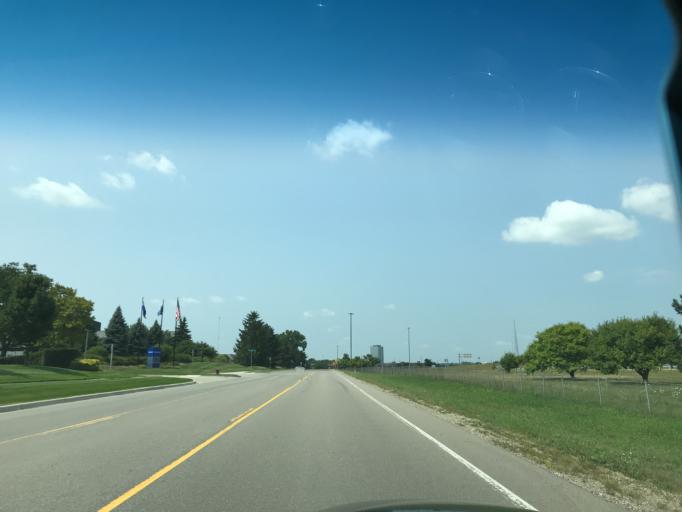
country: US
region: Michigan
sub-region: Oakland County
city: Bingham Farms
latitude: 42.4843
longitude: -83.2689
